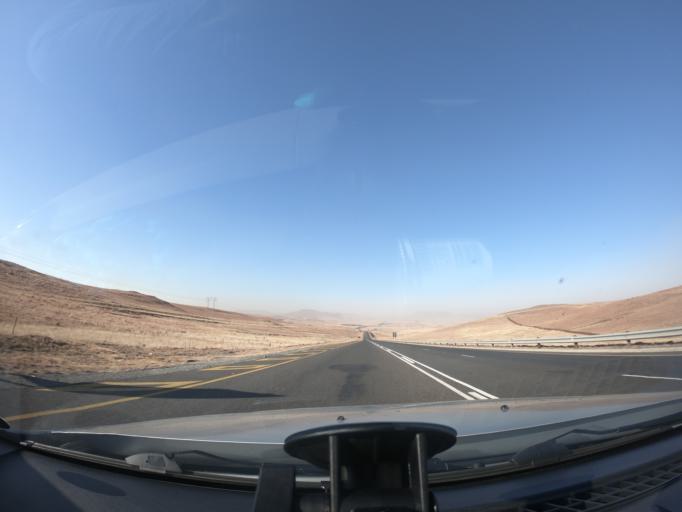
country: ZA
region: Mpumalanga
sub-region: Gert Sibande District Municipality
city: Volksrust
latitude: -27.2030
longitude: 29.8777
